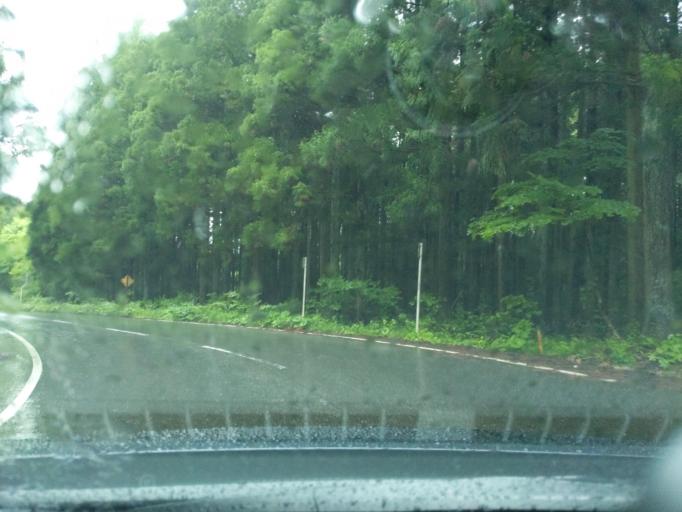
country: JP
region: Fukushima
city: Funehikimachi-funehiki
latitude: 37.6156
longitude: 140.6891
